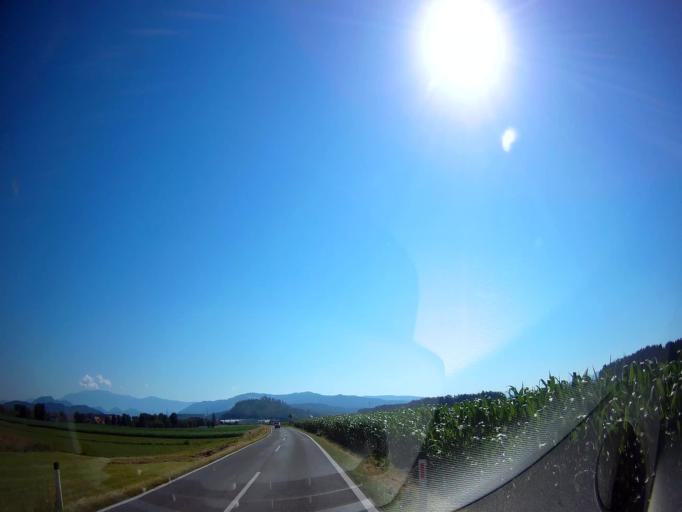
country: AT
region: Carinthia
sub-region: Politischer Bezirk Volkermarkt
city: Globasnitz
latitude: 46.5730
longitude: 14.7169
